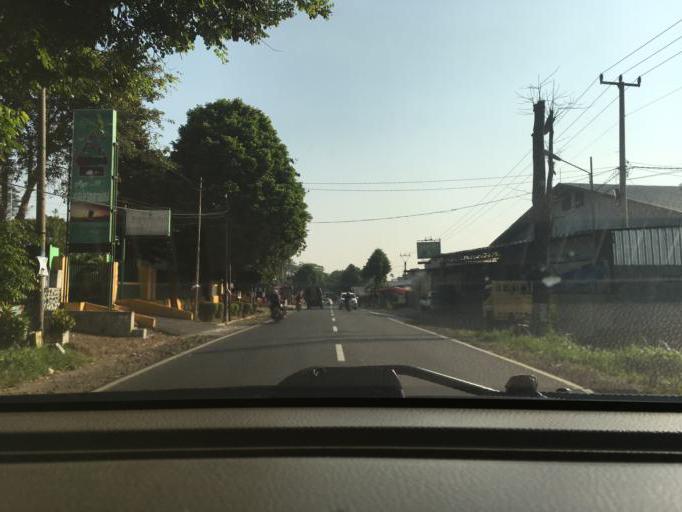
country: ID
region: West Java
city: Kuningan
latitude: -6.9029
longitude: 108.4905
